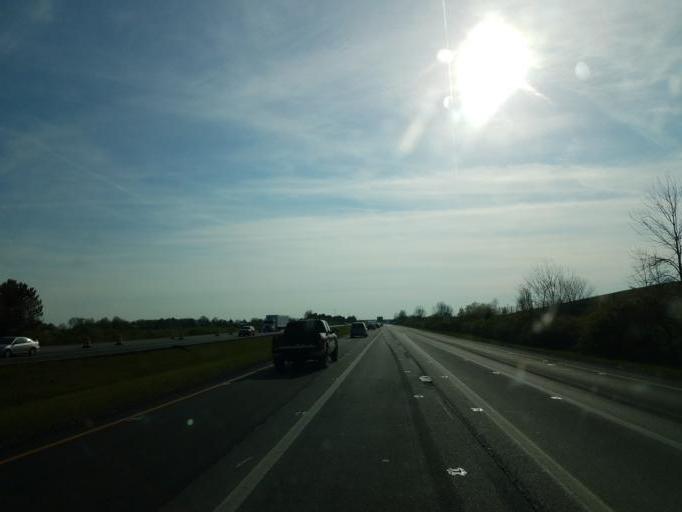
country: US
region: Ohio
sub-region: Franklin County
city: Grove City
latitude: 39.8324
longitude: -83.1054
